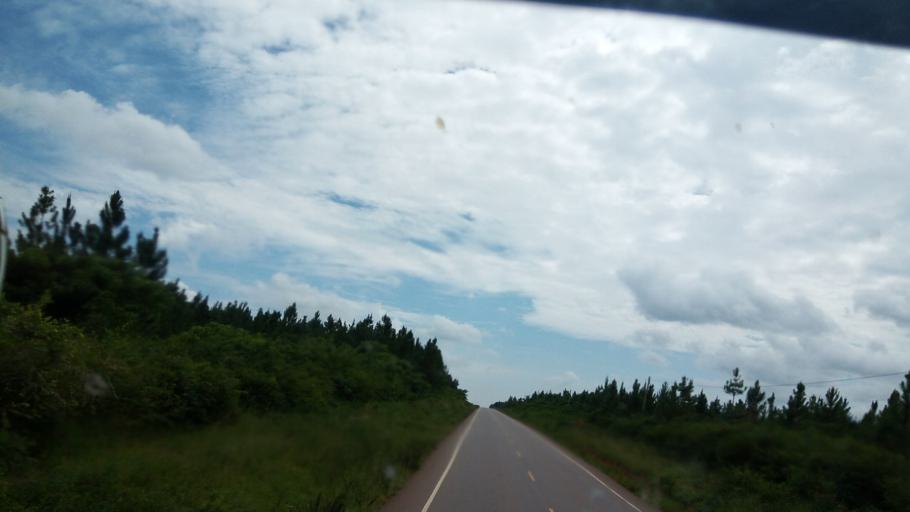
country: UG
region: Central Region
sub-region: Nakasongola District
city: Nakasongola
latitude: 1.1334
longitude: 32.4651
